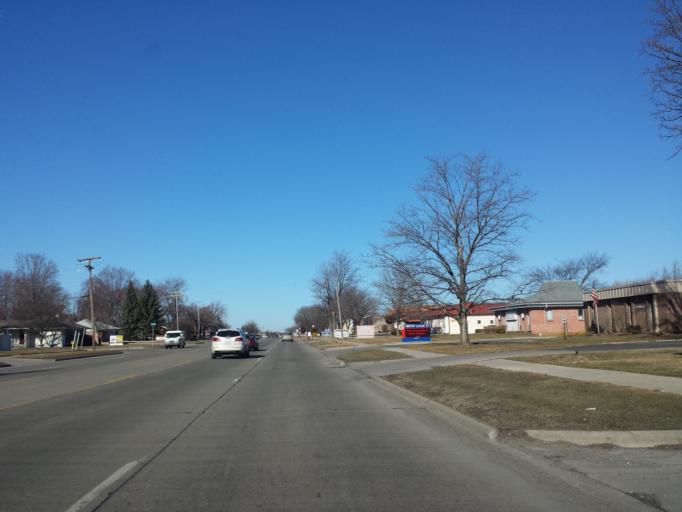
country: US
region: Michigan
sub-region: Oakland County
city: Lathrup Village
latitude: 42.5027
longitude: -83.2138
